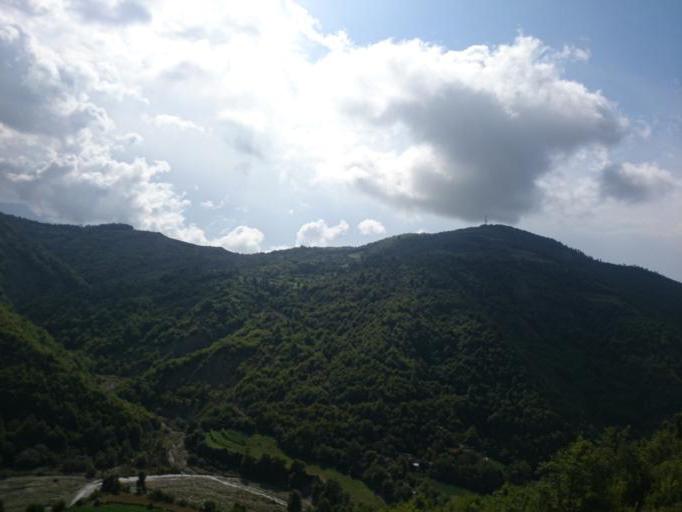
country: AL
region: Elbasan
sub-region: Rrethi i Elbasanit
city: Gjinar
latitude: 40.9786
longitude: 20.2049
